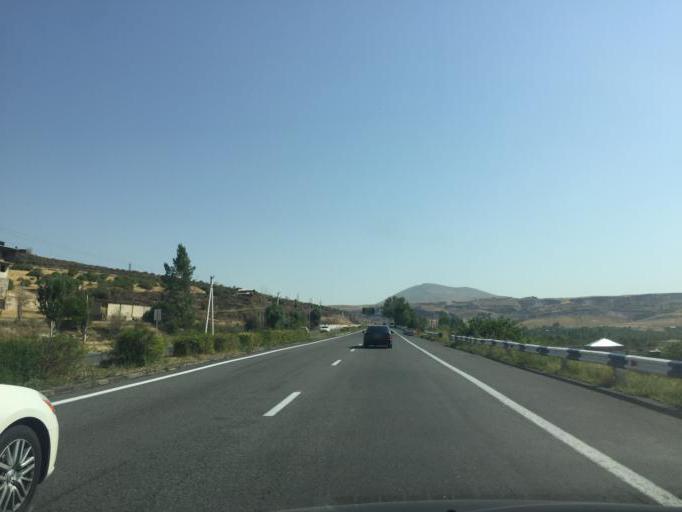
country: AM
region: Kotayk'i Marz
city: Byureghavan
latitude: 40.3151
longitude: 44.6280
